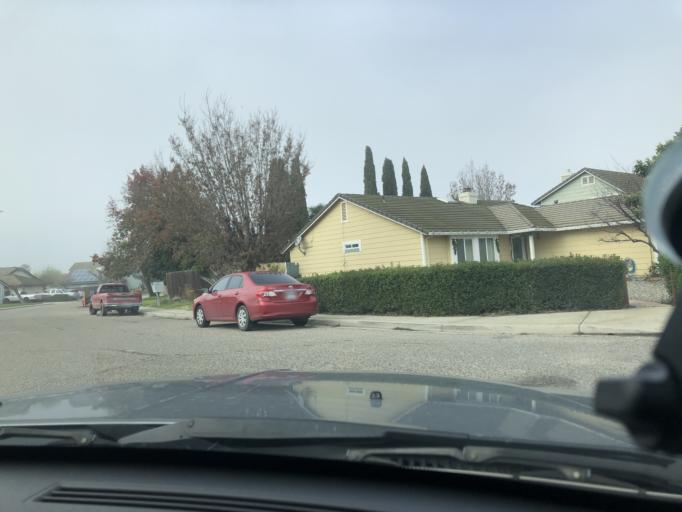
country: US
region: California
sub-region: Monterey County
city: King City
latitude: 36.2133
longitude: -121.1360
